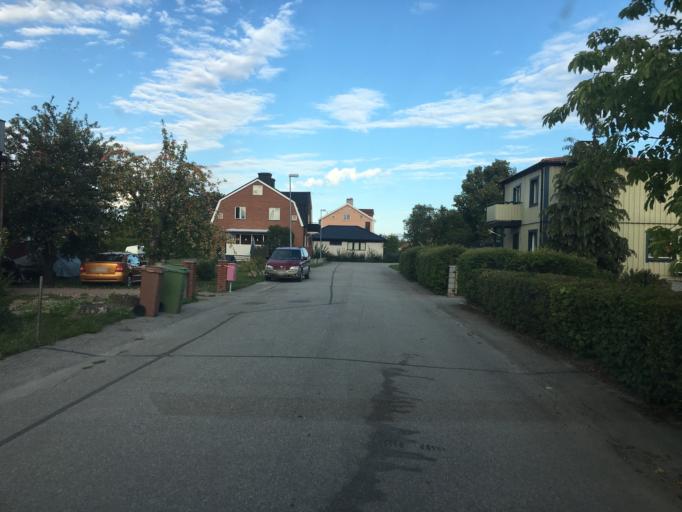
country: SE
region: Vaestmanland
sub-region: Vasteras
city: Tillberga
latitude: 59.6862
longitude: 16.6206
